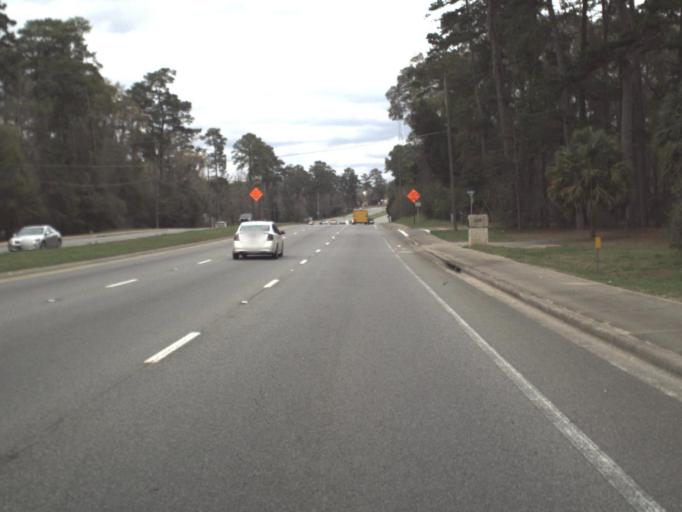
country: US
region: Florida
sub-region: Leon County
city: Tallahassee
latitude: 30.5548
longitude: -84.2216
